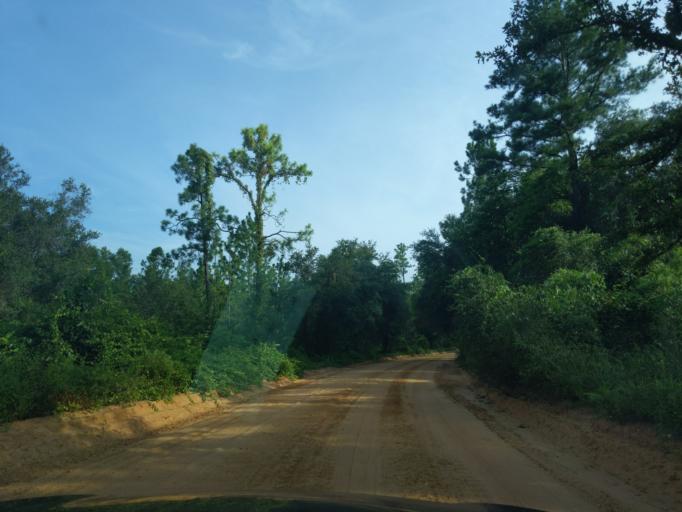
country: US
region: Florida
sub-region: Gadsden County
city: Midway
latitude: 30.3961
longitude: -84.4091
